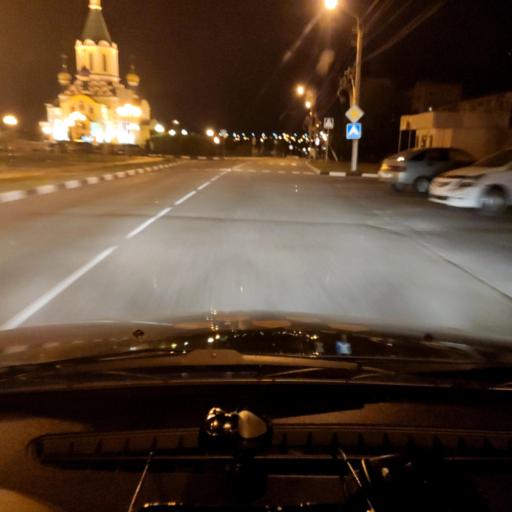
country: RU
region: Belgorod
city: Mayskiy
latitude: 50.5207
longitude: 36.4524
